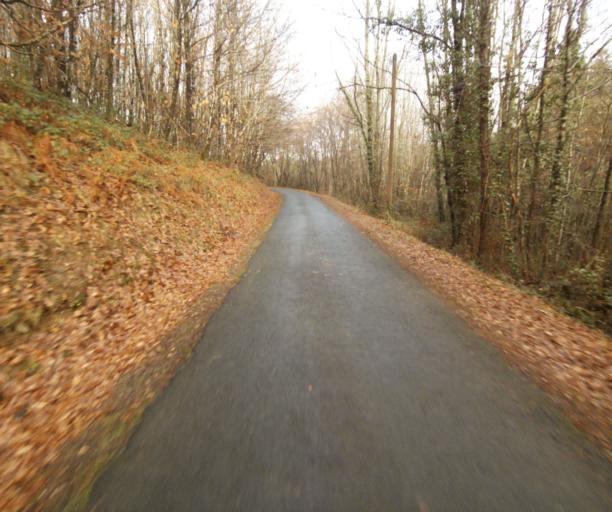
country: FR
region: Limousin
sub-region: Departement de la Correze
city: Saint-Mexant
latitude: 45.2565
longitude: 1.6423
